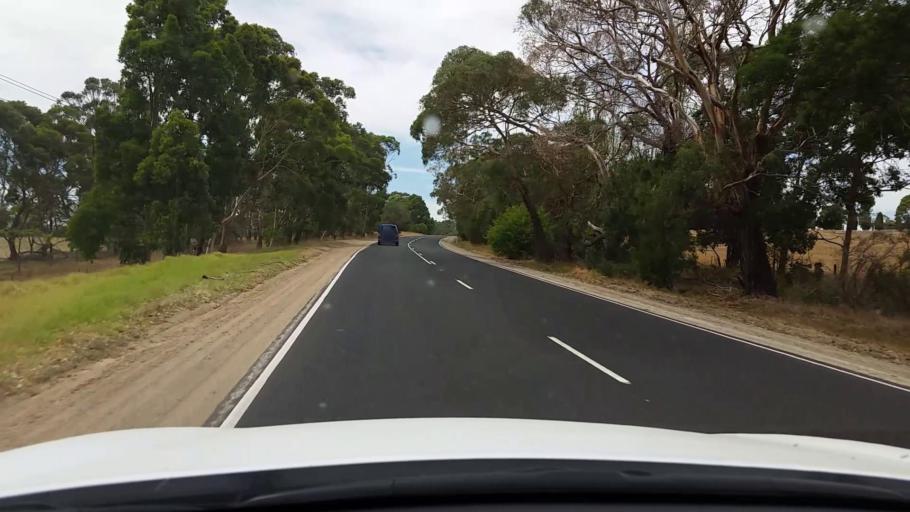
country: AU
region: Victoria
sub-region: Mornington Peninsula
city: Safety Beach
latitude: -38.3075
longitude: 145.0343
